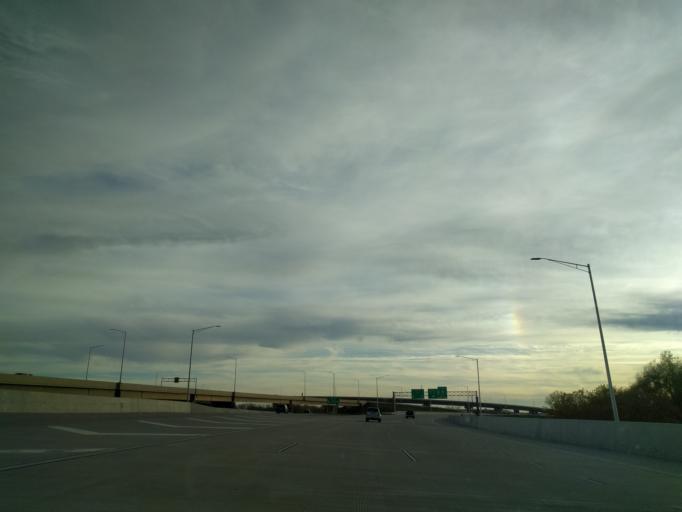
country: US
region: Wisconsin
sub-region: Brown County
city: Howard
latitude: 44.5651
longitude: -88.0496
